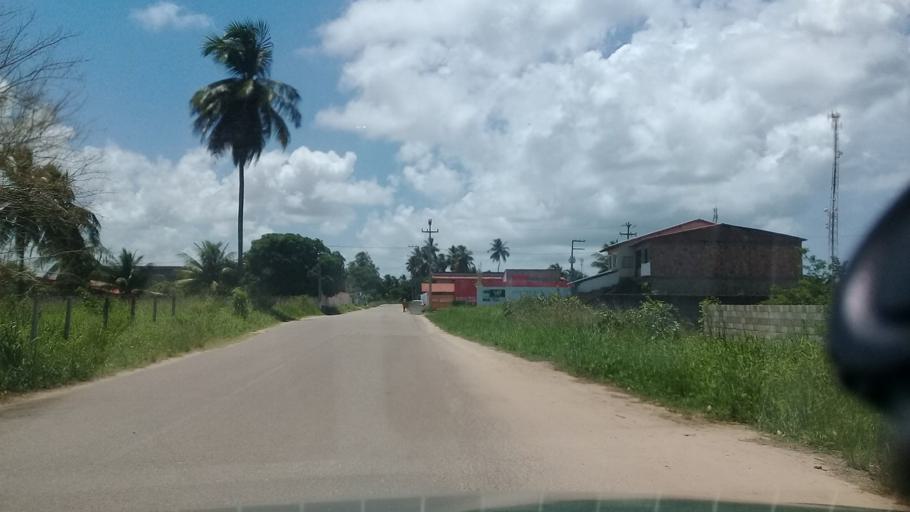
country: BR
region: Pernambuco
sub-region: Sirinhaem
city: Sirinhaem
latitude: -8.6216
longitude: -35.0601
